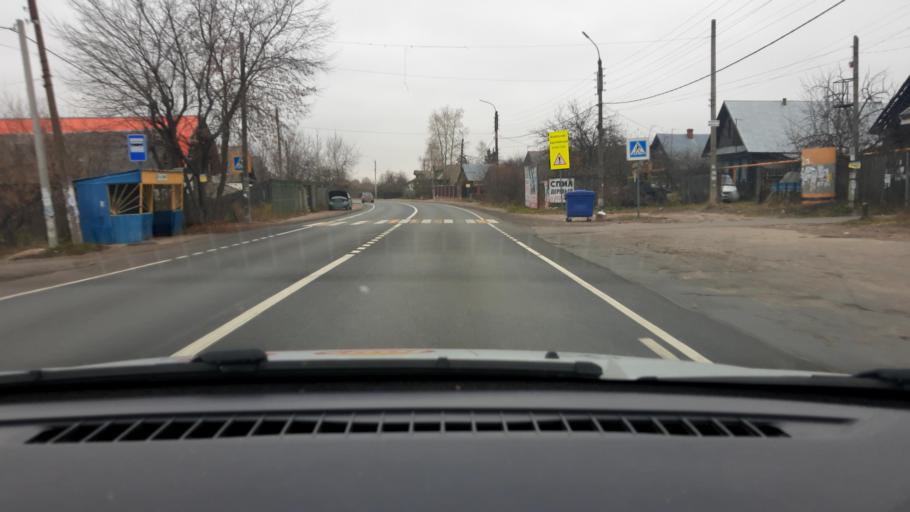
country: RU
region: Nizjnij Novgorod
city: Gidrotorf
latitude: 56.5375
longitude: 43.5367
